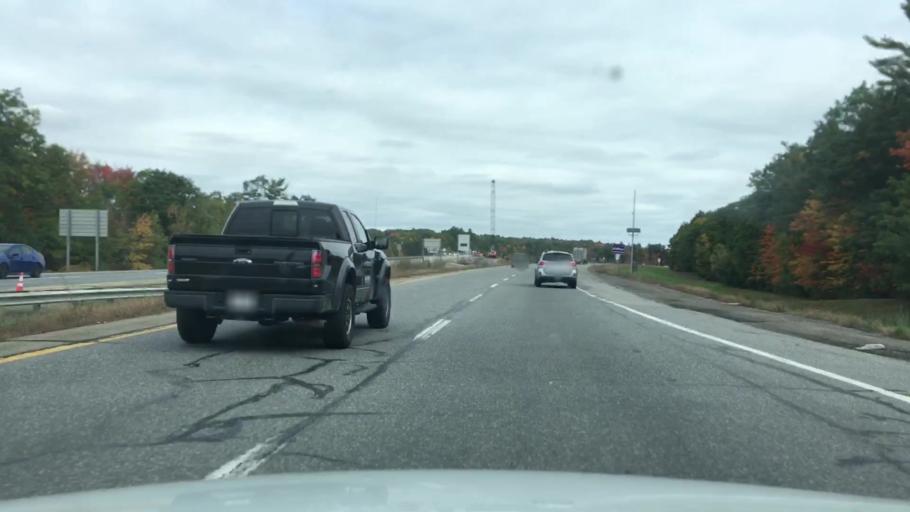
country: US
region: Maine
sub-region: Kennebec County
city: Gardiner
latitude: 44.2137
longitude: -69.8241
